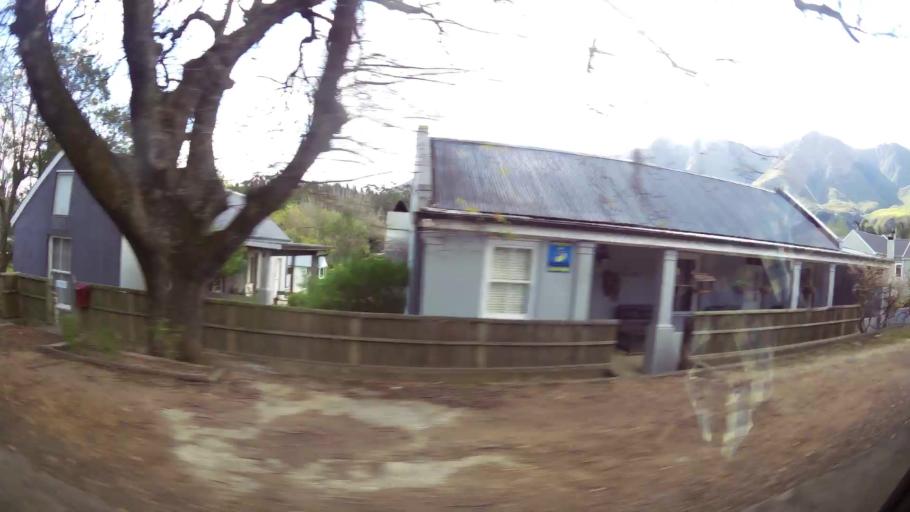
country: ZA
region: Western Cape
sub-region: Overberg District Municipality
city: Swellendam
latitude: -34.0129
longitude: 20.4569
